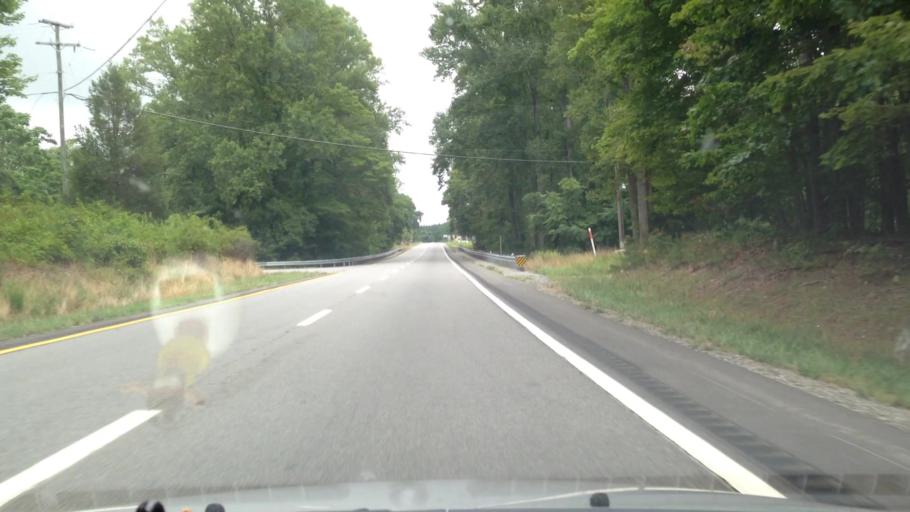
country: US
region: North Carolina
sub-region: Rockingham County
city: Stoneville
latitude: 36.5581
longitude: -79.8874
